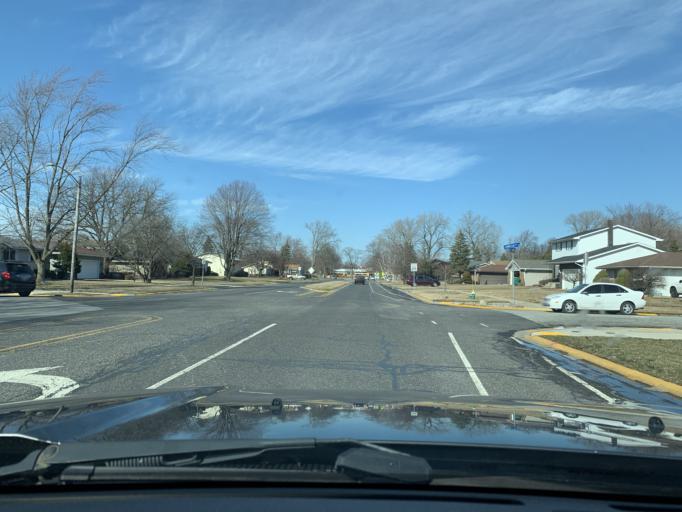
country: US
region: Indiana
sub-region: Lake County
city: Munster
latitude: 41.5398
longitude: -87.4996
